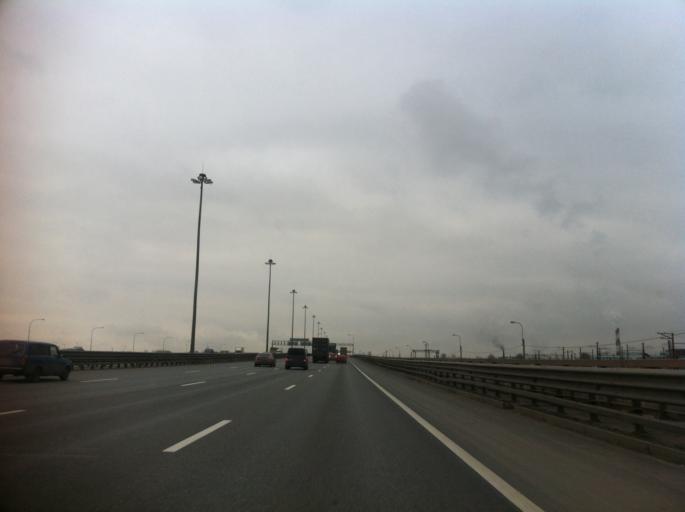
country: RU
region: St.-Petersburg
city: Dachnoye
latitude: 59.8187
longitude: 30.3071
